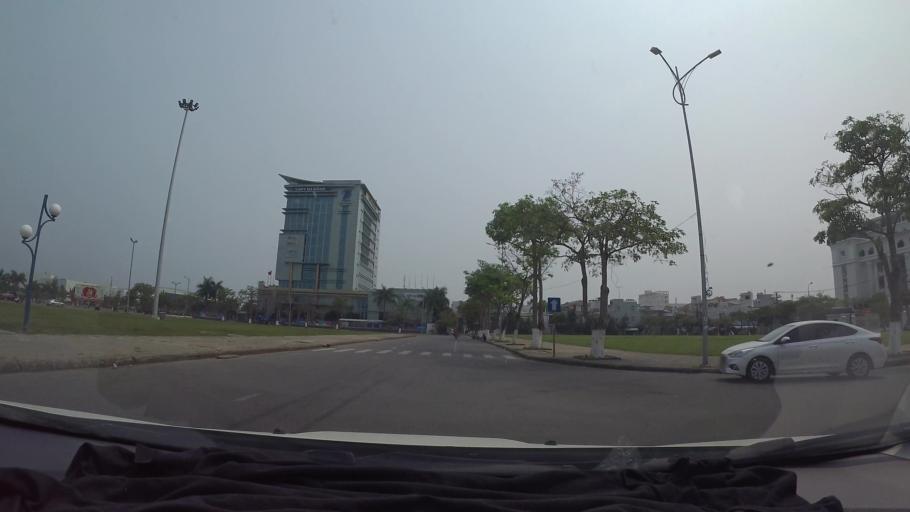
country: VN
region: Da Nang
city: Son Tra
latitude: 16.0407
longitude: 108.2225
